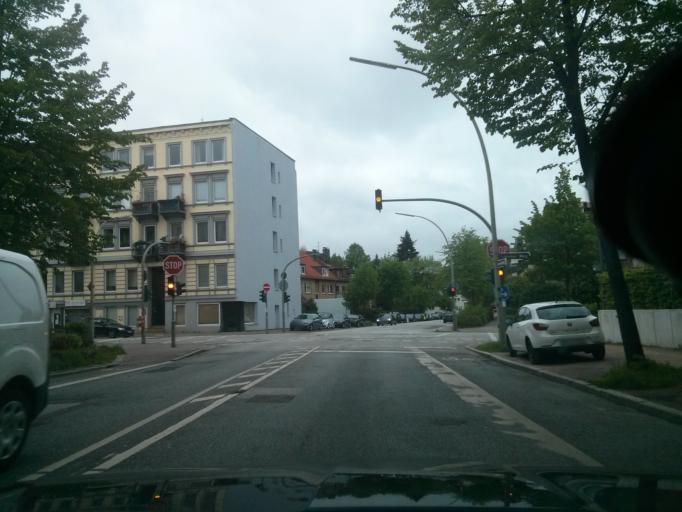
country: DE
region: Hamburg
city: Borgfelde
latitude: 53.5683
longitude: 10.0437
